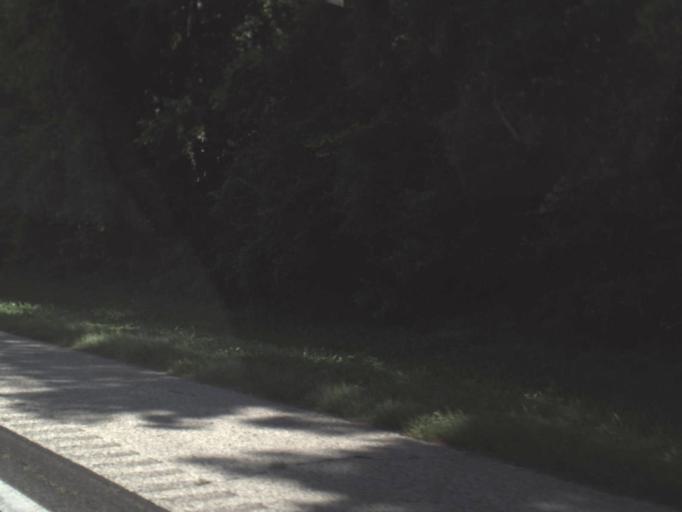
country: US
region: Florida
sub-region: Alachua County
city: Alachua
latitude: 29.7572
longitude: -82.4977
